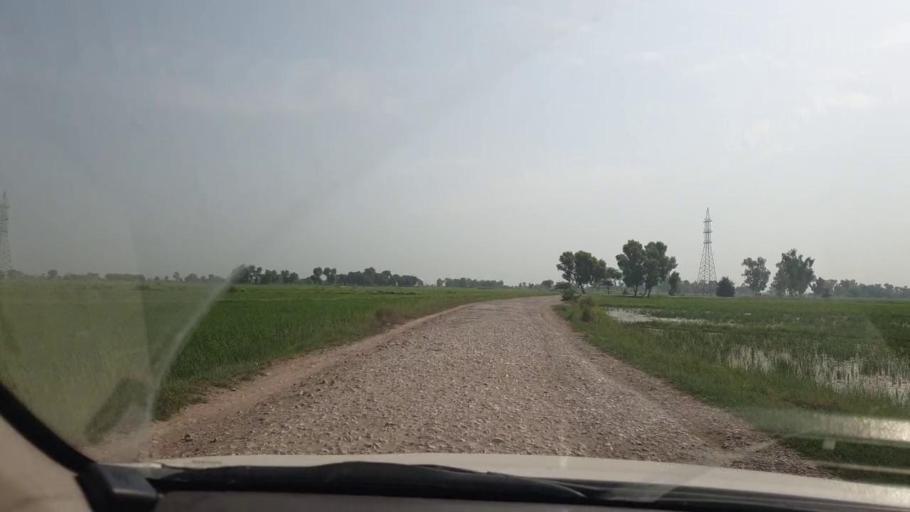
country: PK
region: Sindh
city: Lakhi
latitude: 27.8271
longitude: 68.7343
